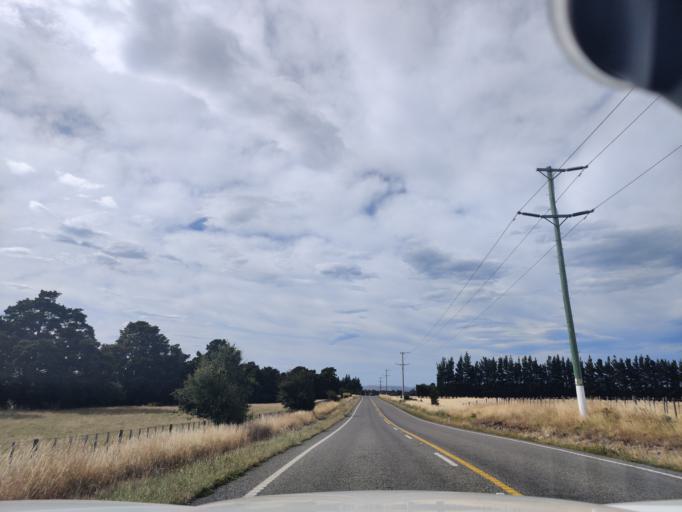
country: NZ
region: Wellington
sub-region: Masterton District
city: Masterton
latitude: -40.8372
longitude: 175.6296
